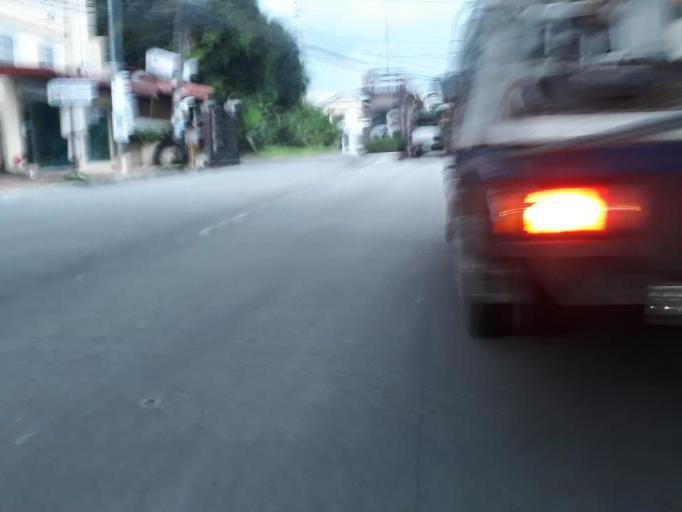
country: PH
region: Metro Manila
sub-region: Quezon City
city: Quezon City
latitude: 14.6856
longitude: 121.0777
